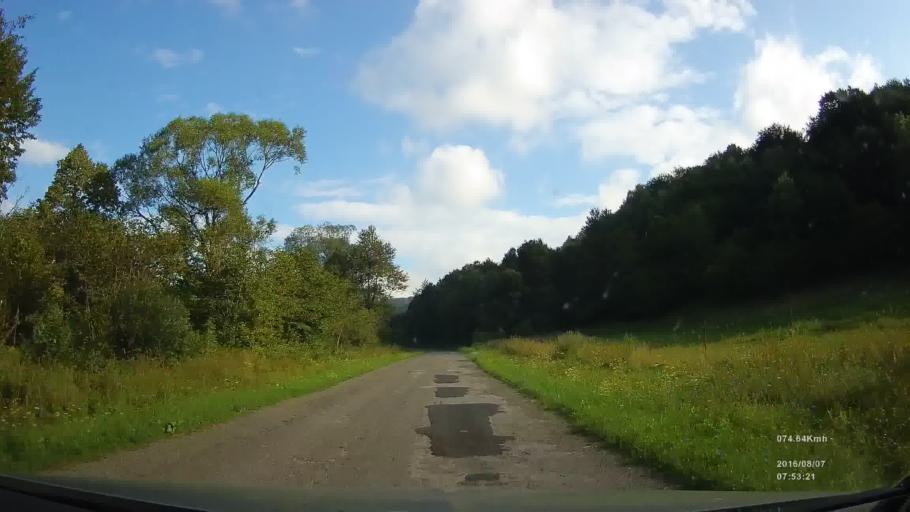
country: SK
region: Presovsky
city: Medzilaborce
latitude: 49.3164
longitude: 21.7960
